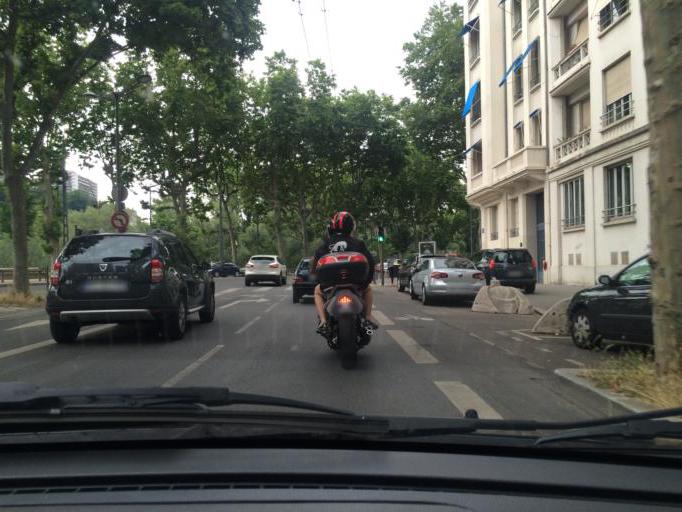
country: FR
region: Rhone-Alpes
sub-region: Departement du Rhone
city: Caluire-et-Cuire
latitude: 45.7744
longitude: 4.8428
